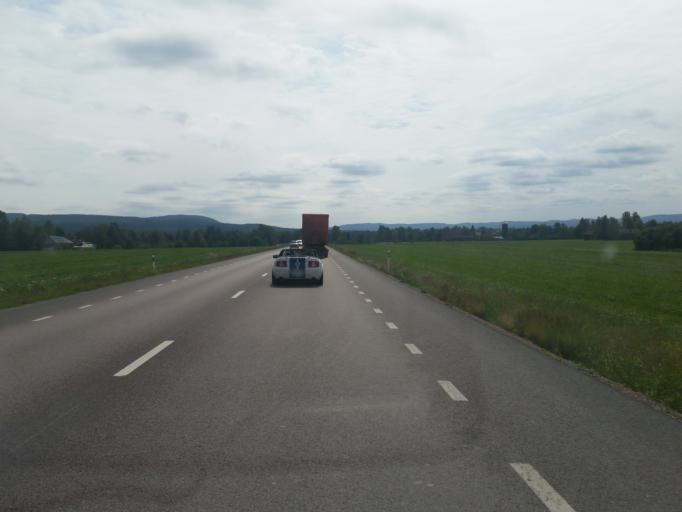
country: SE
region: Dalarna
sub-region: Gagnefs Kommun
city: Gagnef
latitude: 60.5875
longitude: 15.0923
